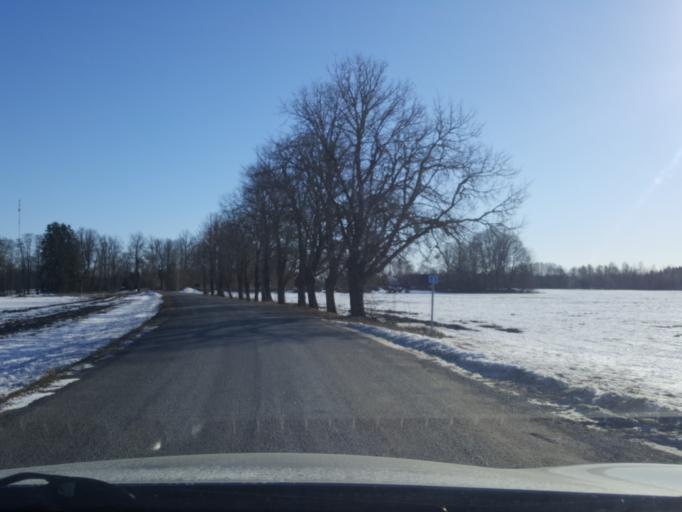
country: EE
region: Viljandimaa
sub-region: Viljandi linn
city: Viljandi
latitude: 58.4615
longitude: 25.5832
